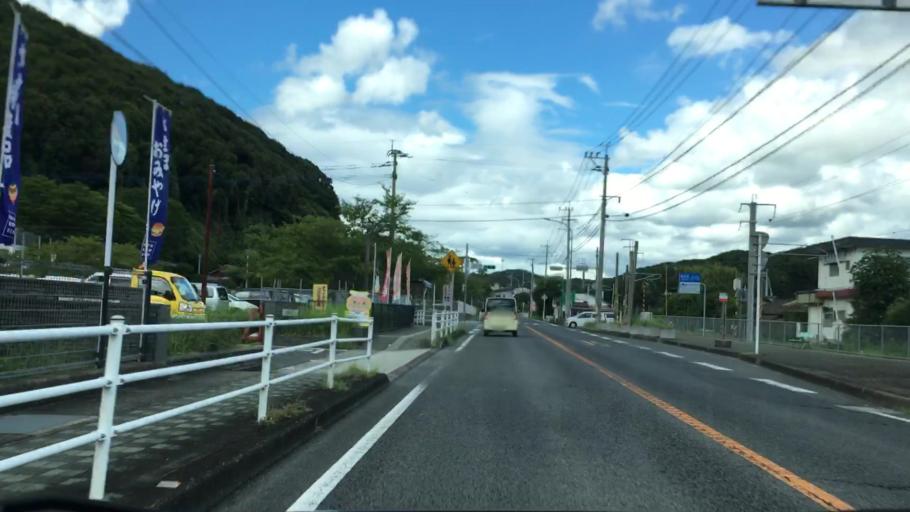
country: JP
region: Nagasaki
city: Sasebo
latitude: 33.1526
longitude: 129.8298
